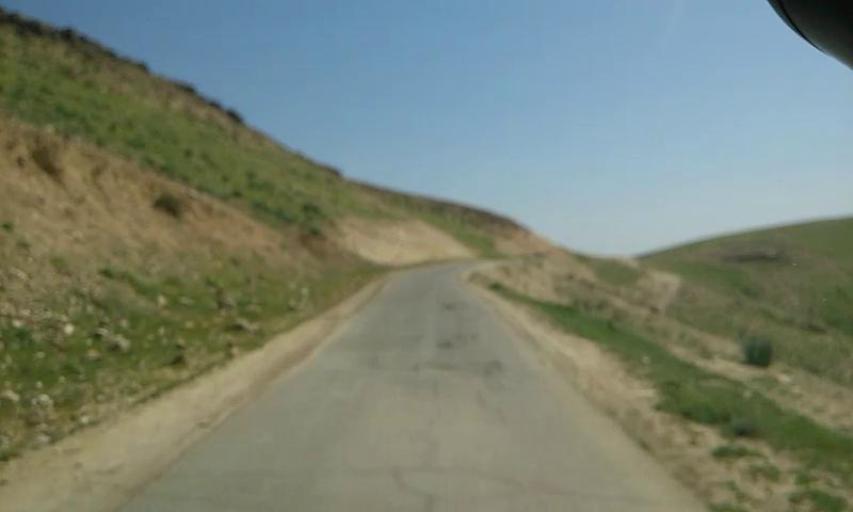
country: PS
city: `Arab ar Rashaydah
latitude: 31.5615
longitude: 35.2439
